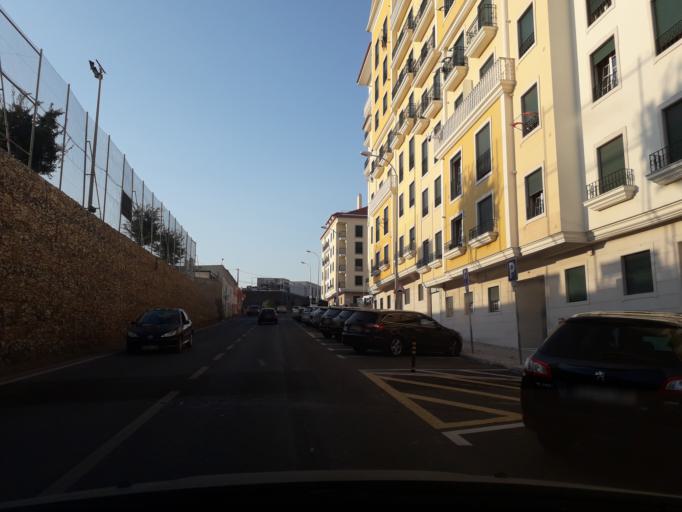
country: PT
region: Lisbon
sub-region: Amadora
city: Amadora
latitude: 38.7435
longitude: -9.2264
